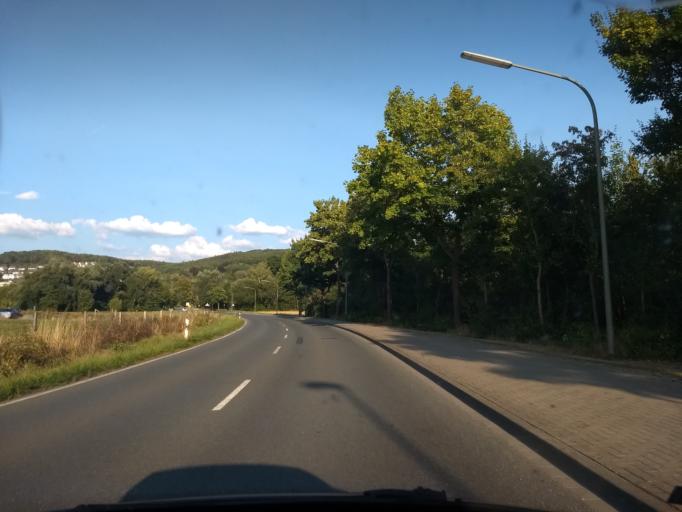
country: DE
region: North Rhine-Westphalia
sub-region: Regierungsbezirk Arnsberg
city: Arnsberg
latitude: 51.3821
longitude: 8.0652
